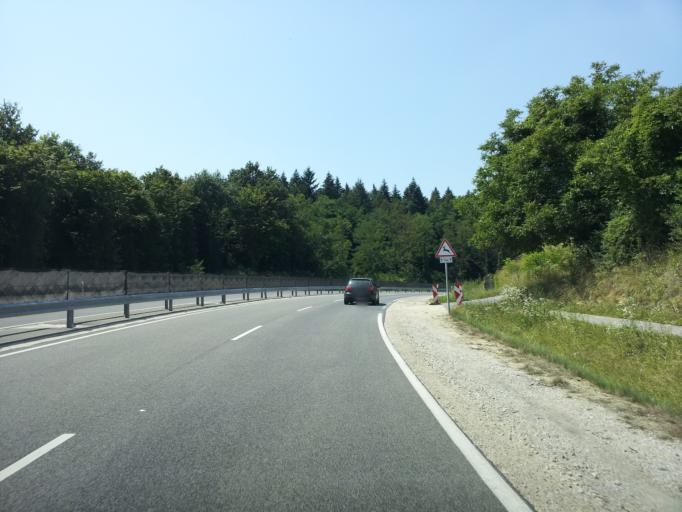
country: HU
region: Zala
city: Zalaegerszeg
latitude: 46.8410
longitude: 16.9013
